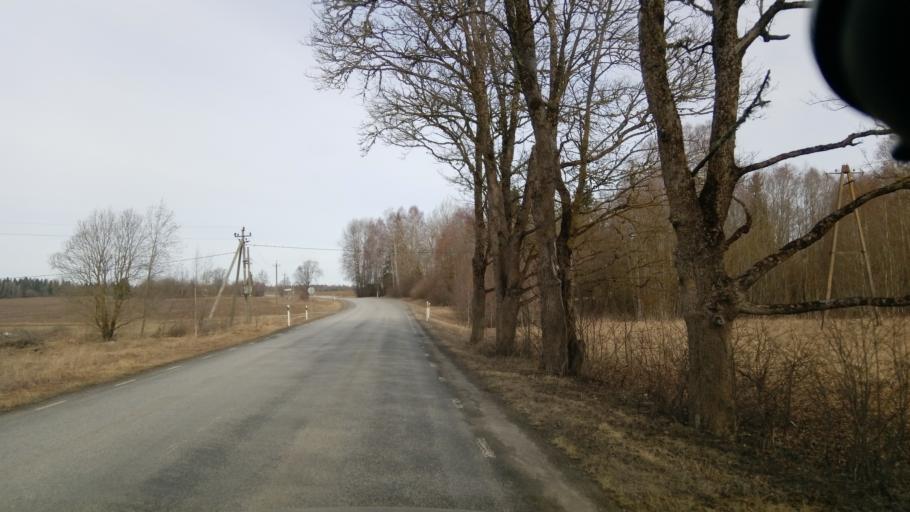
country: EE
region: Raplamaa
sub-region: Rapla vald
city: Rapla
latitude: 59.0249
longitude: 24.8385
